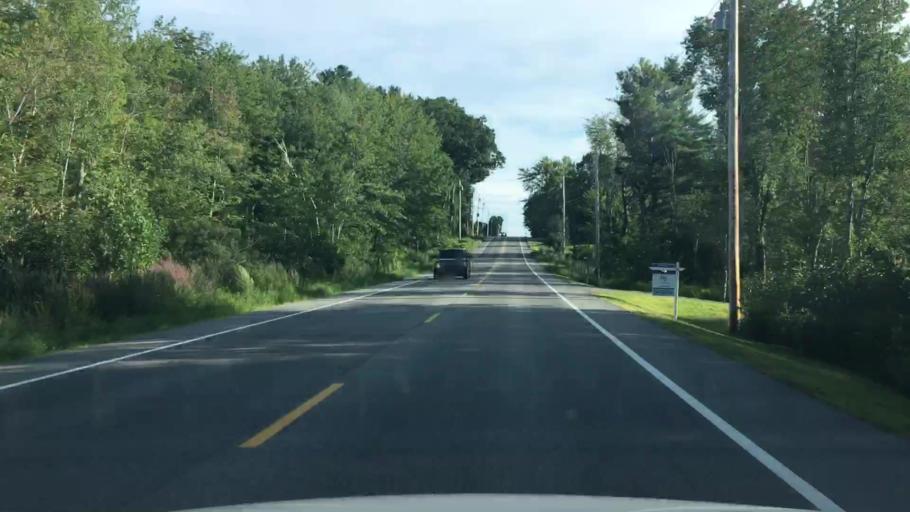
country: US
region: Maine
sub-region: Cumberland County
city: North Windham
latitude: 43.7914
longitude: -70.4399
